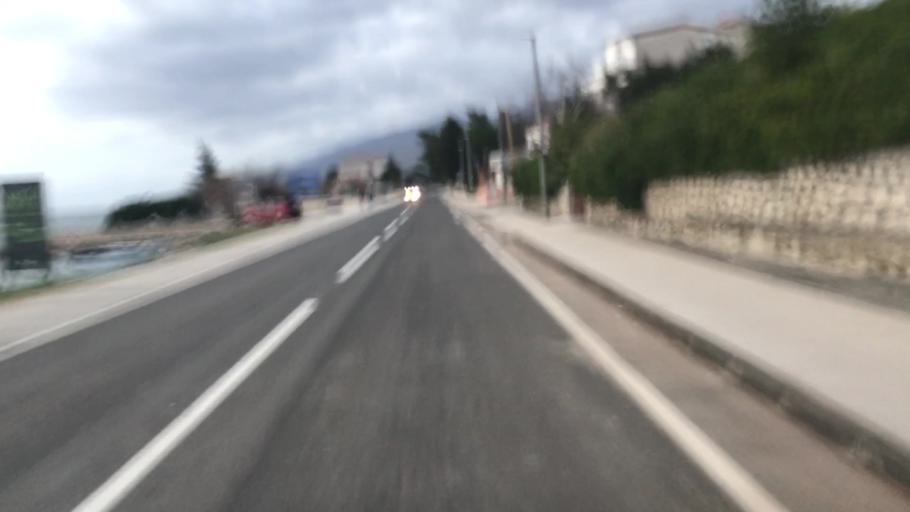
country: HR
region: Zadarska
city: Starigrad
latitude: 44.2896
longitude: 15.4444
